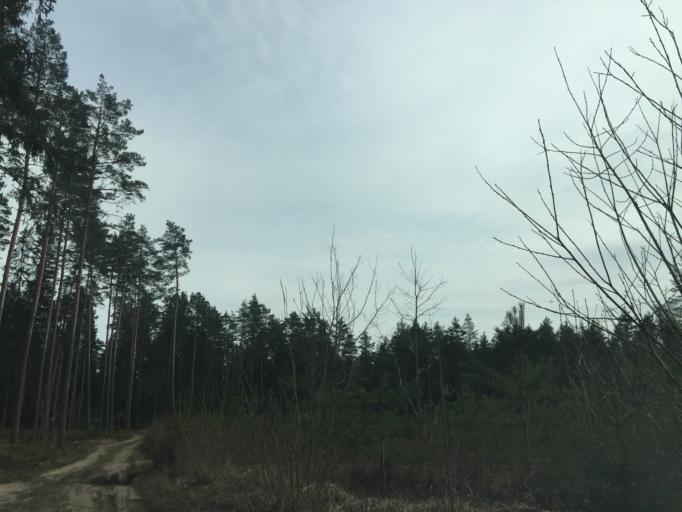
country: LV
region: Sigulda
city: Sigulda
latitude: 57.1322
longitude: 24.8033
